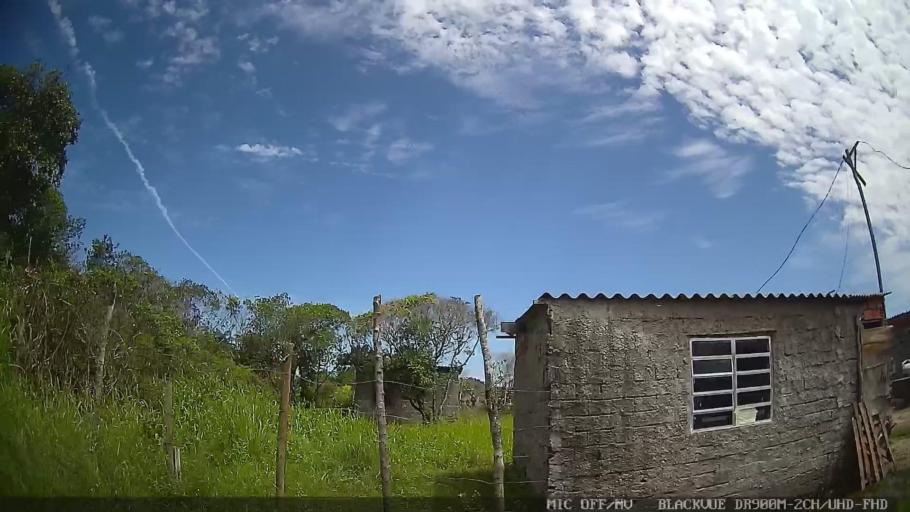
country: BR
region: Sao Paulo
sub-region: Iguape
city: Iguape
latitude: -24.7193
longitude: -47.5271
